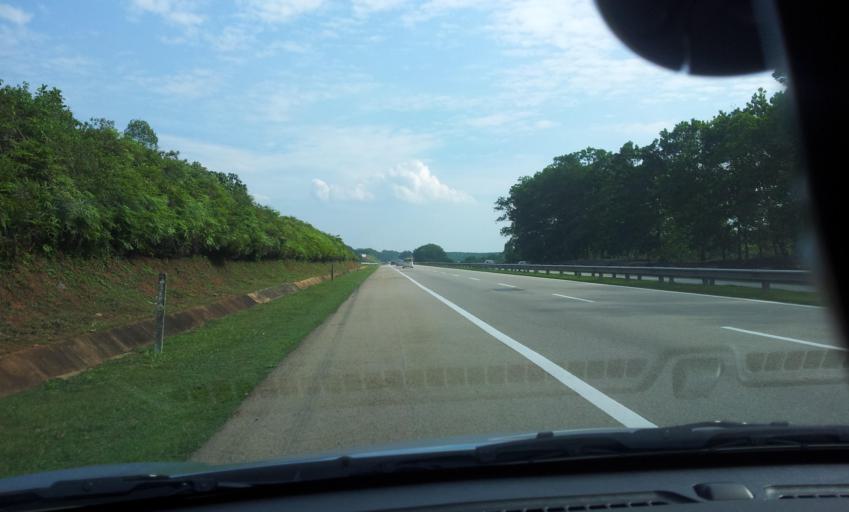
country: MY
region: Pahang
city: Temerluh
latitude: 3.5687
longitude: 102.5578
